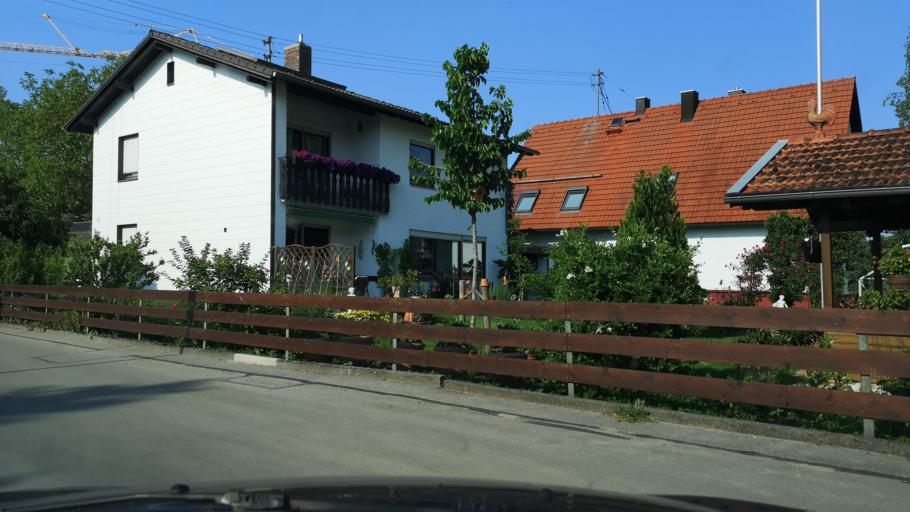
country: DE
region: Bavaria
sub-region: Upper Bavaria
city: Poing
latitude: 48.1716
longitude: 11.8148
